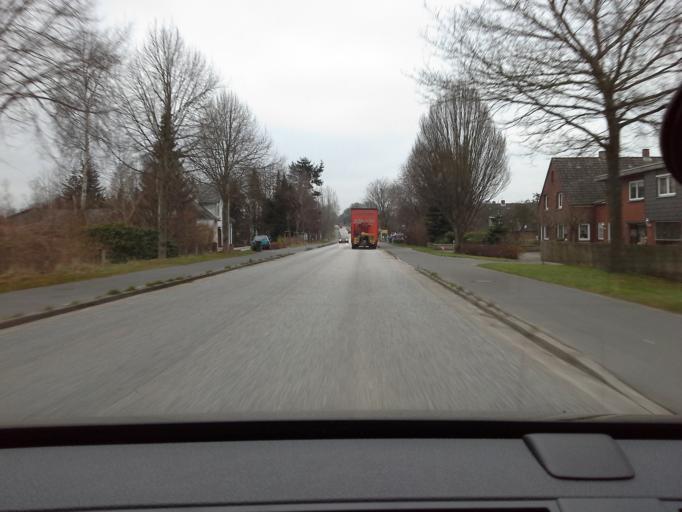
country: DE
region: Schleswig-Holstein
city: Lentfohrden
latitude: 53.8699
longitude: 9.8887
